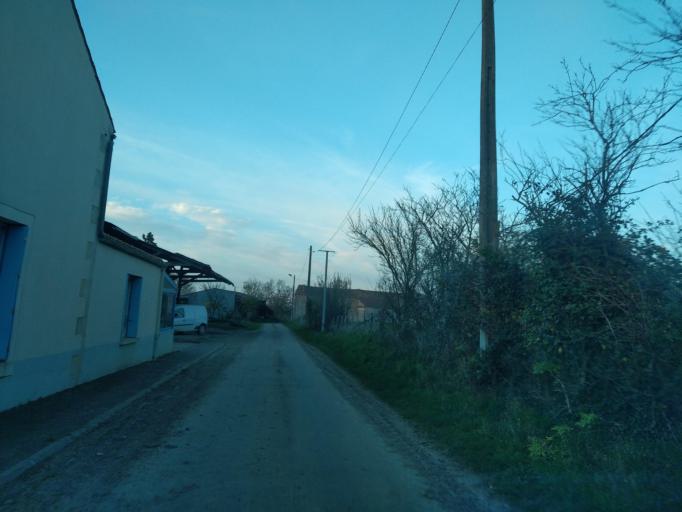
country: FR
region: Pays de la Loire
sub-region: Departement de la Vendee
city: Maillezais
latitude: 46.3596
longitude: -0.7365
